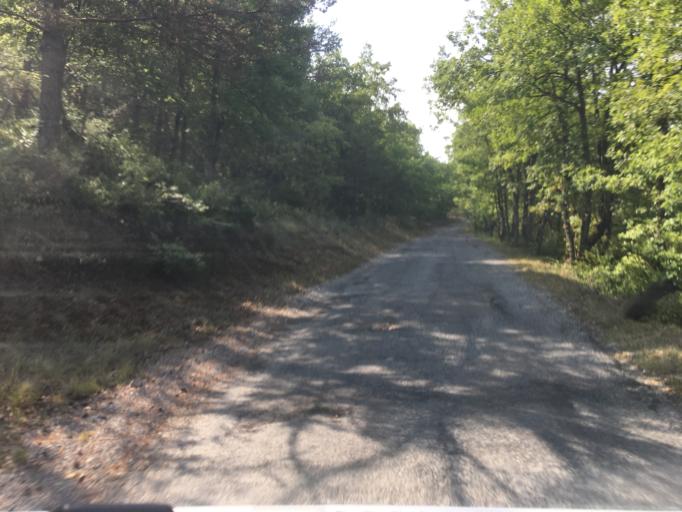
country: FR
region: Provence-Alpes-Cote d'Azur
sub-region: Departement des Alpes-de-Haute-Provence
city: Mallemoisson
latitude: 43.9245
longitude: 6.1917
